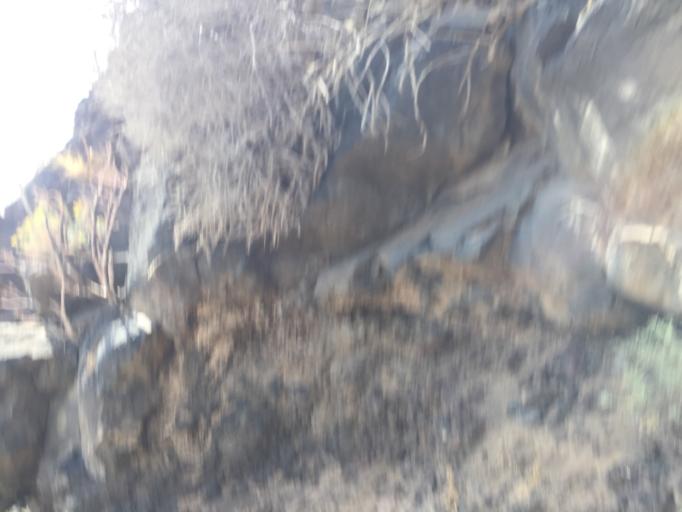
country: ES
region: Canary Islands
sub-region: Provincia de Santa Cruz de Tenerife
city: Tazacorte
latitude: 28.6532
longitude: -17.9474
